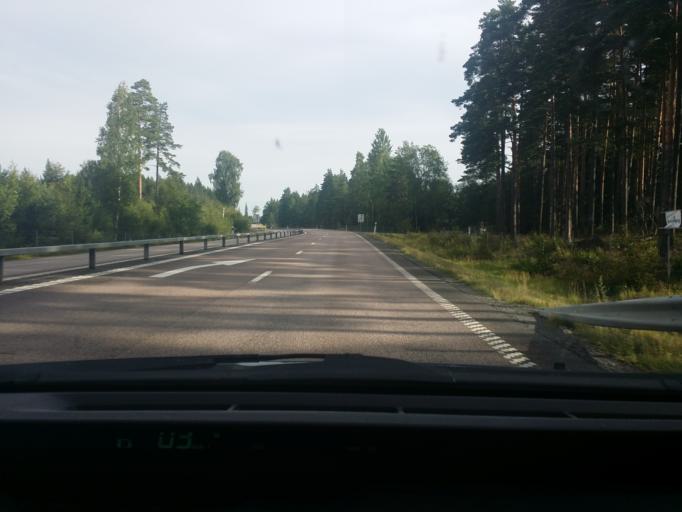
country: SE
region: Vaestmanland
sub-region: Vasteras
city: Tillberga
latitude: 59.7828
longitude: 16.5671
